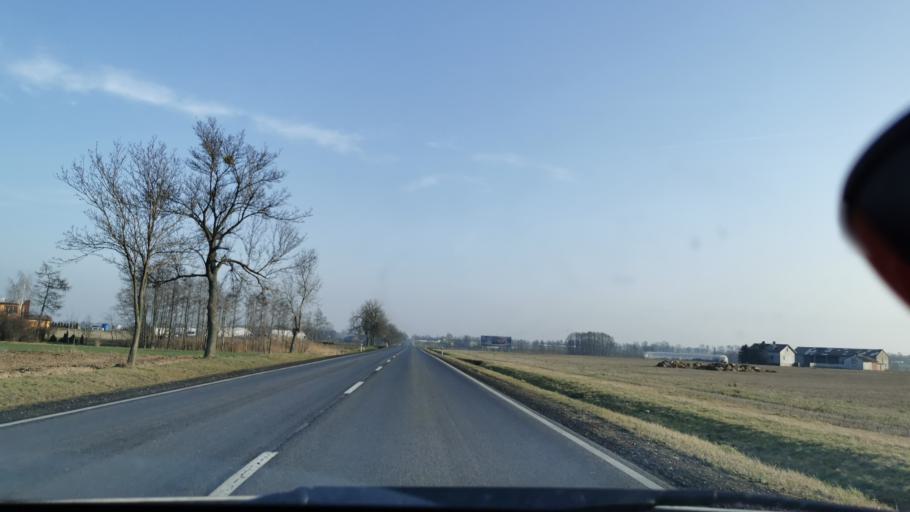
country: PL
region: Lodz Voivodeship
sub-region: Powiat sieradzki
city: Blaszki
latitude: 51.6804
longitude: 18.3436
